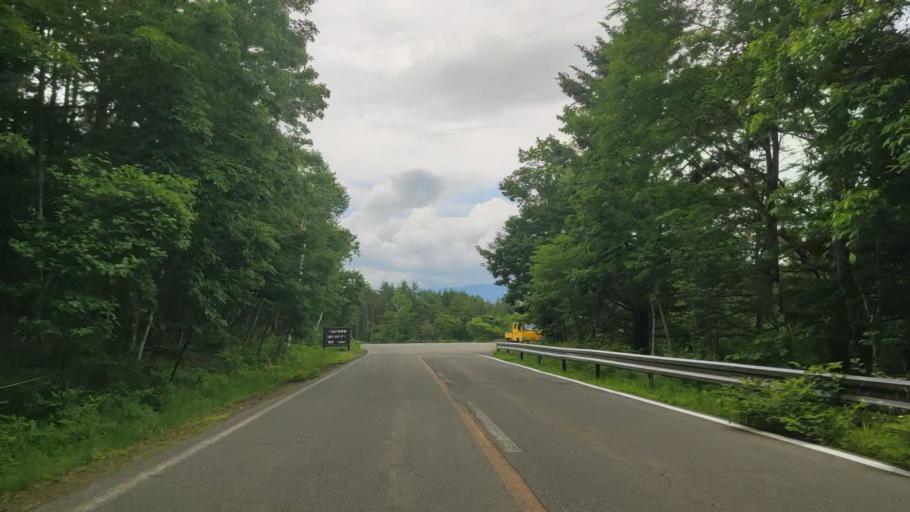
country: JP
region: Yamanashi
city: Fujikawaguchiko
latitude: 35.4294
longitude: 138.7390
